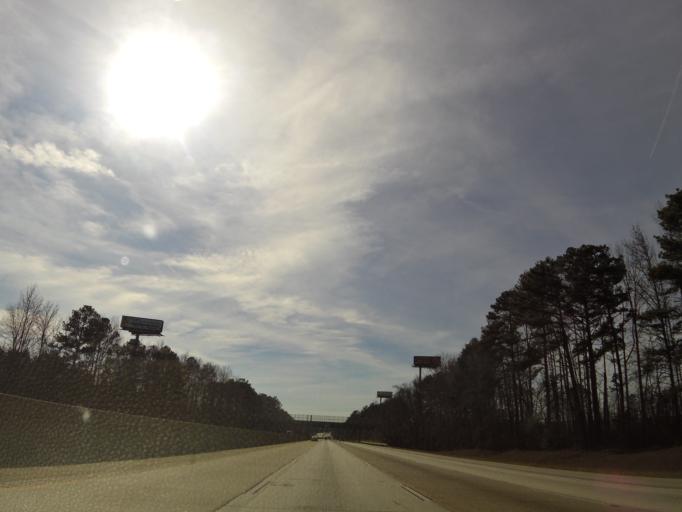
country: US
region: Georgia
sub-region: Fulton County
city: Fairburn
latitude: 33.5403
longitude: -84.5895
